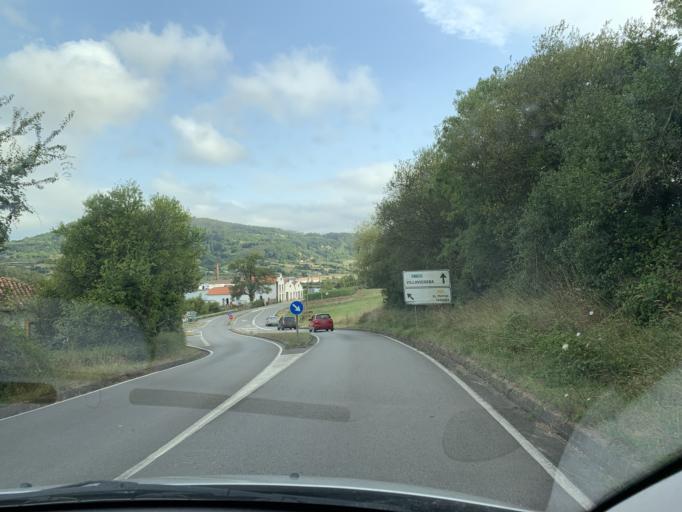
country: ES
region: Asturias
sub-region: Province of Asturias
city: Villaviciosa
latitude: 43.5014
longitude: -5.4272
